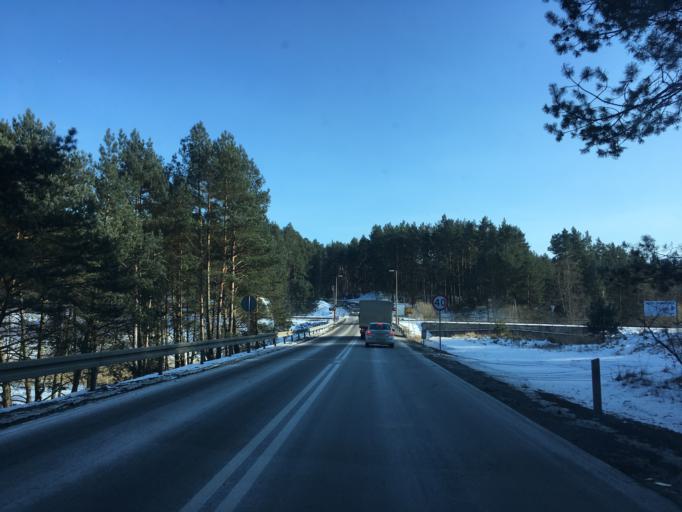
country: PL
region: Pomeranian Voivodeship
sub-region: Powiat koscierski
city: Koscierzyna
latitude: 54.1188
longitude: 17.8884
